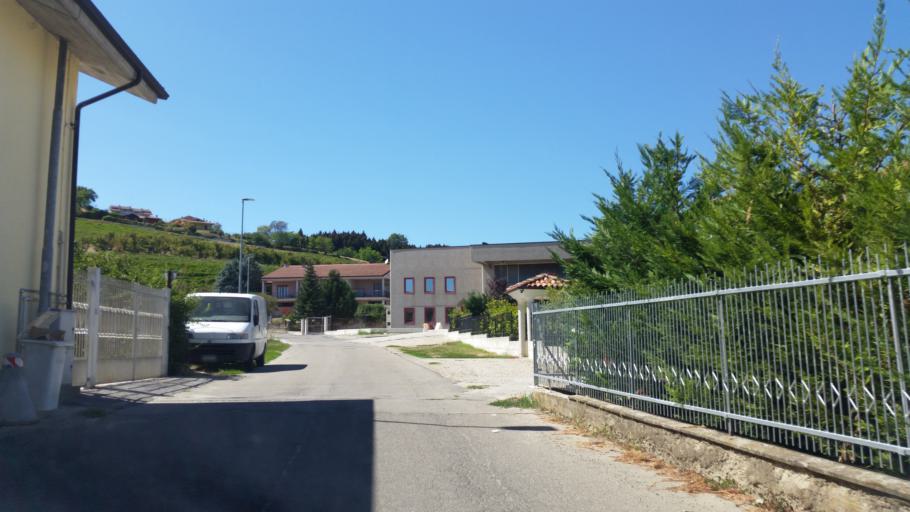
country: IT
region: Piedmont
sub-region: Provincia di Cuneo
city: Neive-Borgonovo
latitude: 44.7286
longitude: 8.1221
